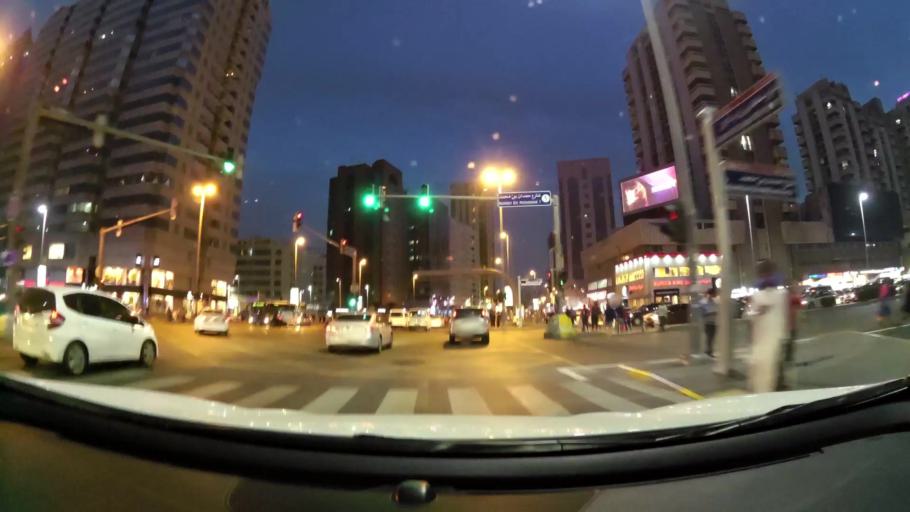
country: AE
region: Abu Dhabi
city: Abu Dhabi
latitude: 24.4899
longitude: 54.3632
